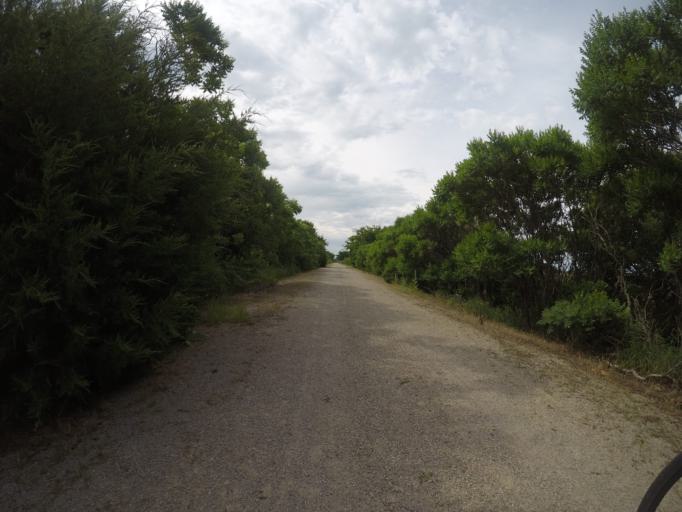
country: US
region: Kansas
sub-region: Anderson County
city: Garnett
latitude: 38.4263
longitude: -95.2633
